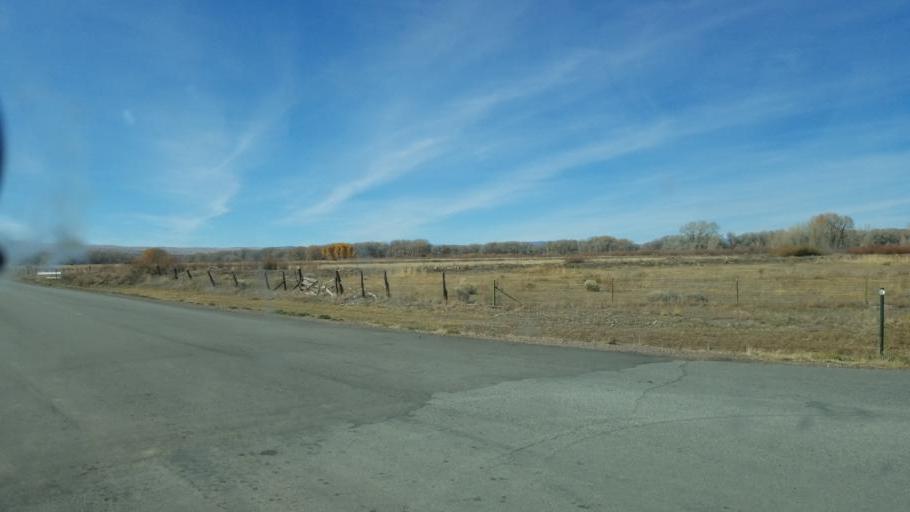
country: US
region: Colorado
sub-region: Conejos County
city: Conejos
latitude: 37.0902
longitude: -106.0093
